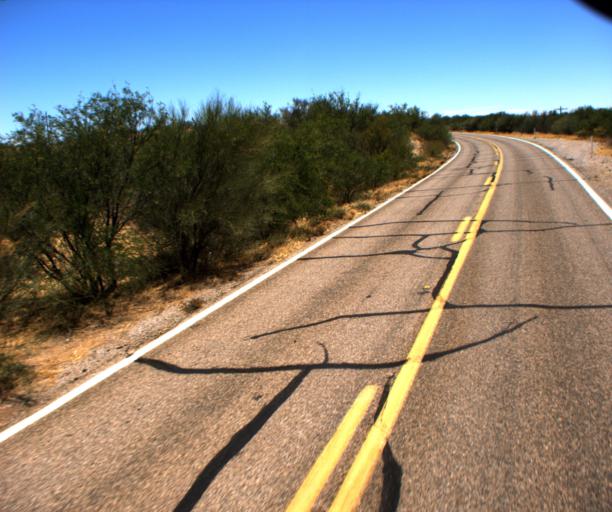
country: US
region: Arizona
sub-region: Pima County
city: Three Points
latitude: 31.9428
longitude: -111.3909
